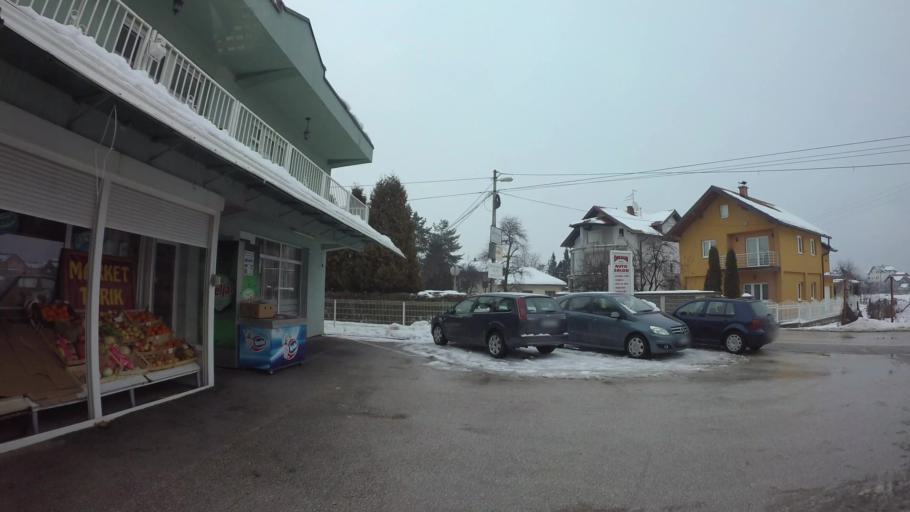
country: BA
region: Federation of Bosnia and Herzegovina
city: Hadzici
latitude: 43.8353
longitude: 18.2791
